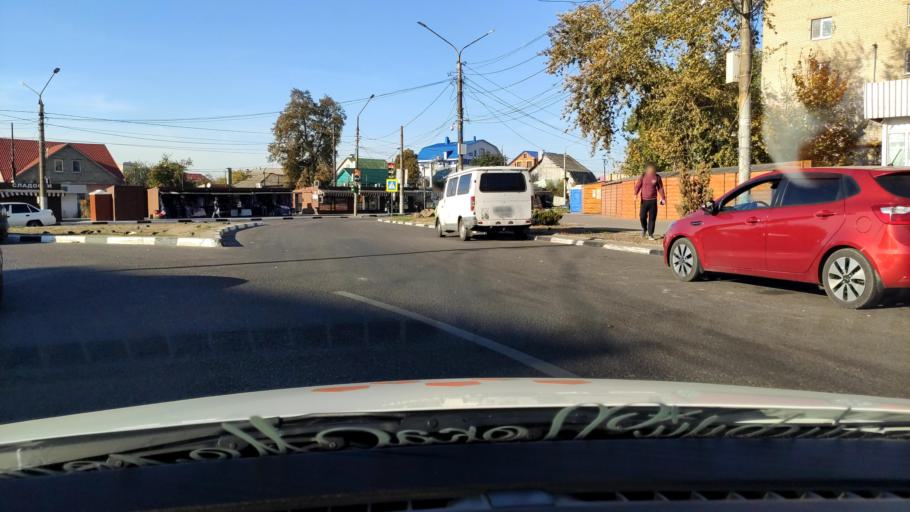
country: RU
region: Voronezj
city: Voronezh
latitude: 51.6359
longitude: 39.1729
